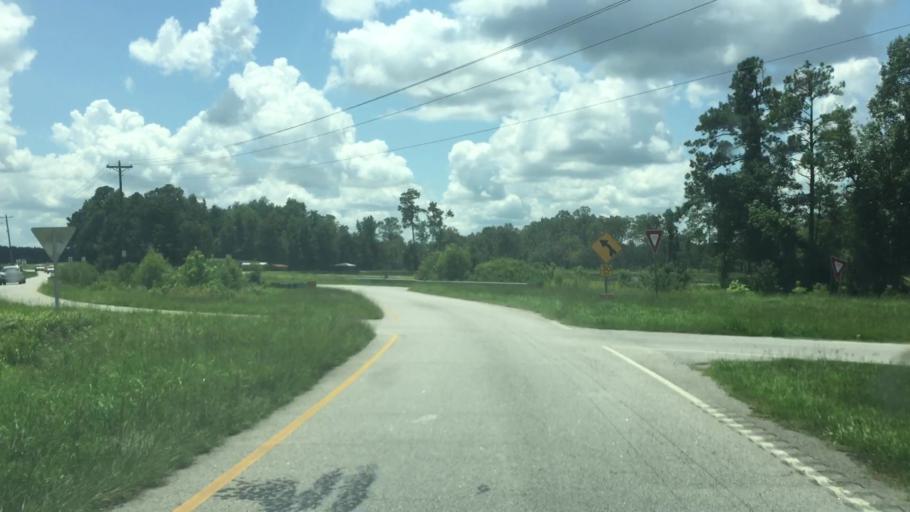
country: US
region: North Carolina
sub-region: Columbus County
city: Tabor City
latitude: 34.1332
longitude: -78.8758
